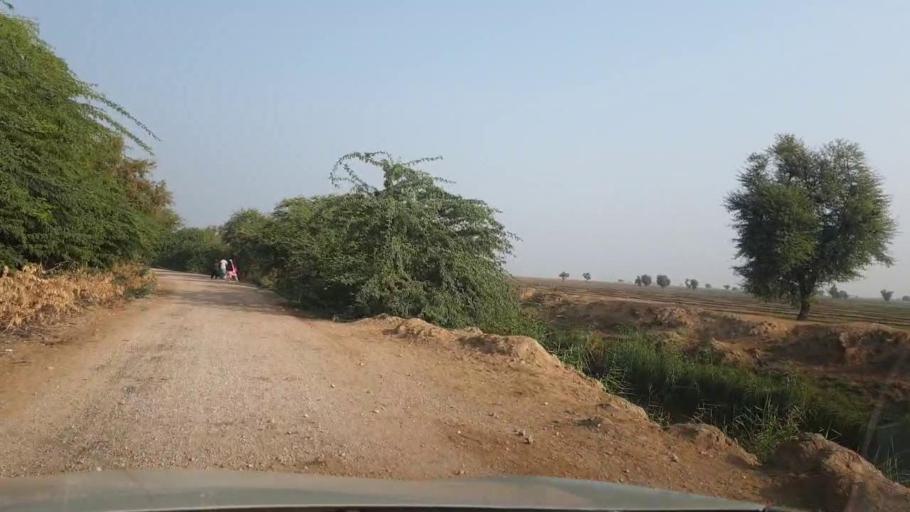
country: PK
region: Sindh
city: Sehwan
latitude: 26.3473
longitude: 67.7234
